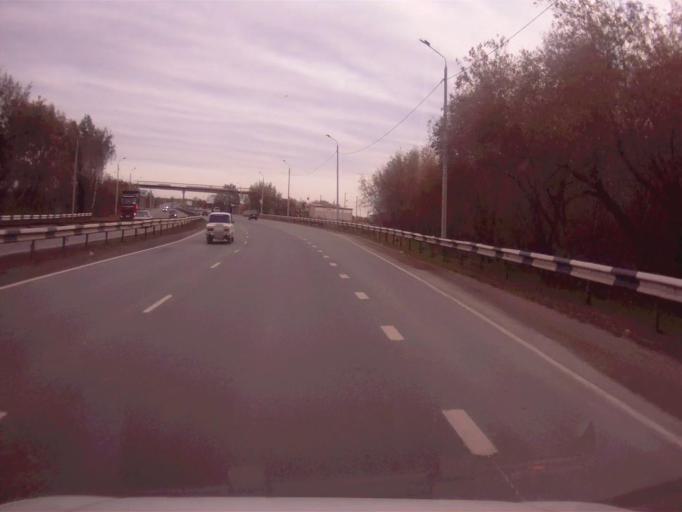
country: RU
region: Chelyabinsk
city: Novosineglazovskiy
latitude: 55.0432
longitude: 61.4250
